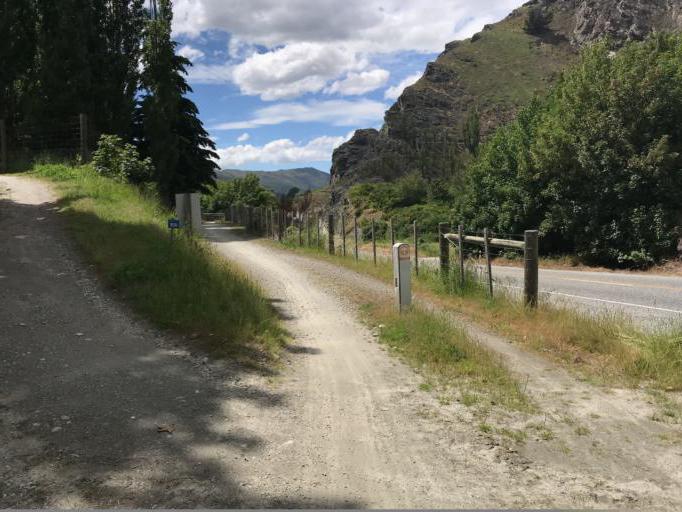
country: NZ
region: Otago
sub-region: Queenstown-Lakes District
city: Arrowtown
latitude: -45.0094
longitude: 168.8944
